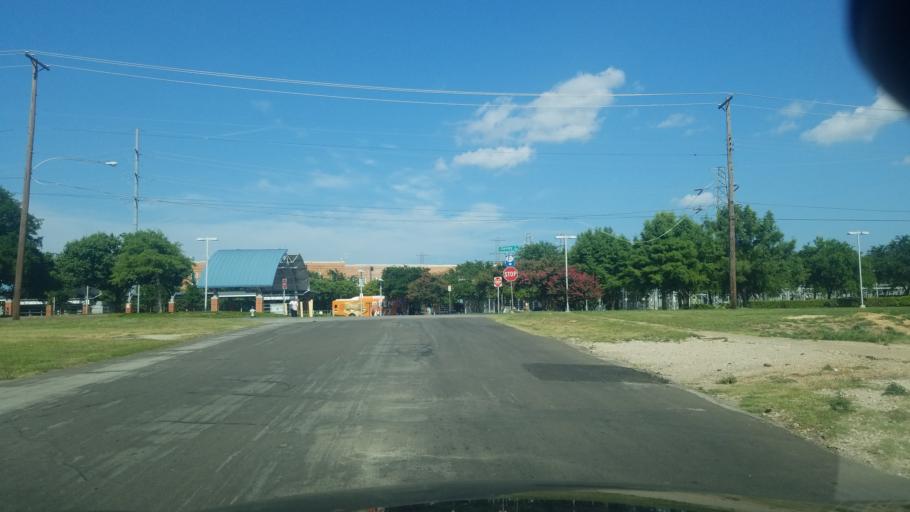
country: US
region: Texas
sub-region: Dallas County
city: Dallas
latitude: 32.7227
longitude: -96.8062
